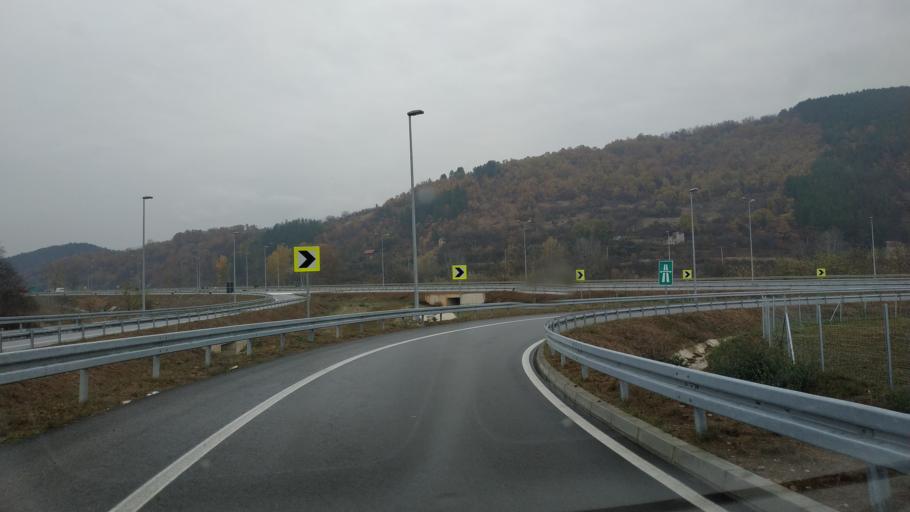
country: RS
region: Central Serbia
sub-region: Pirotski Okrug
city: Pirot
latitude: 43.1908
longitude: 22.5628
